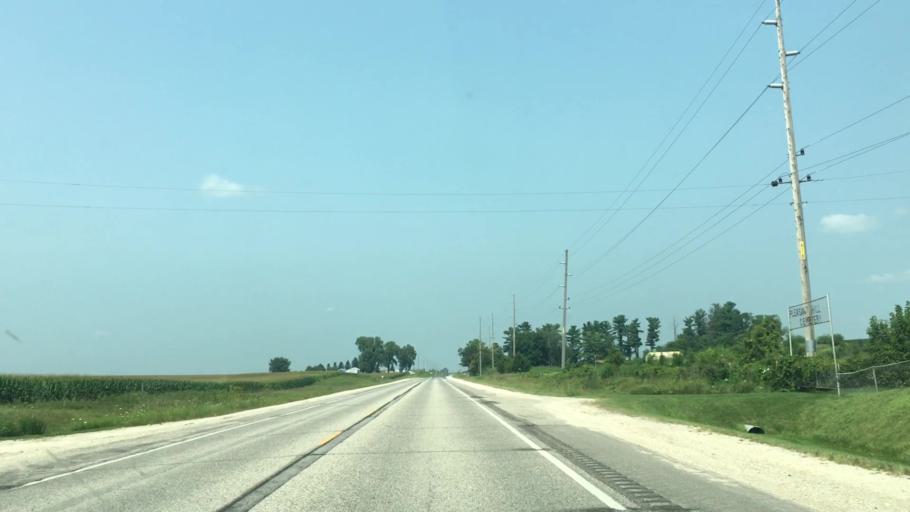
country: US
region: Iowa
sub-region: Fayette County
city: Fayette
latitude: 42.8772
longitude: -91.8105
